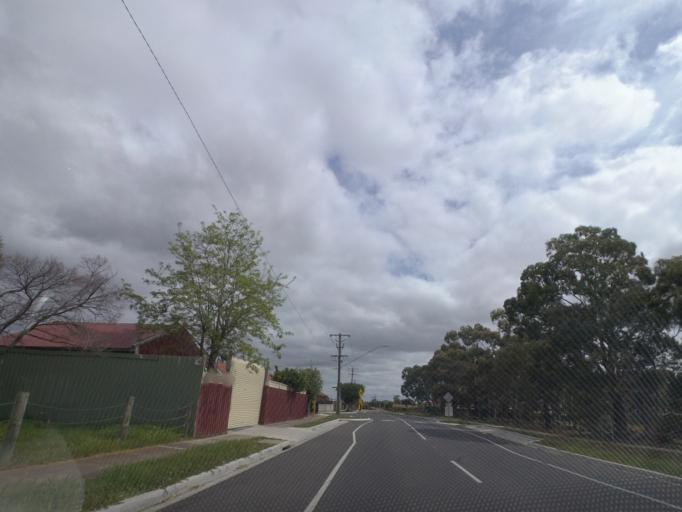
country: AU
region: Victoria
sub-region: Brimbank
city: Deer Park
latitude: -37.7574
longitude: 144.7626
